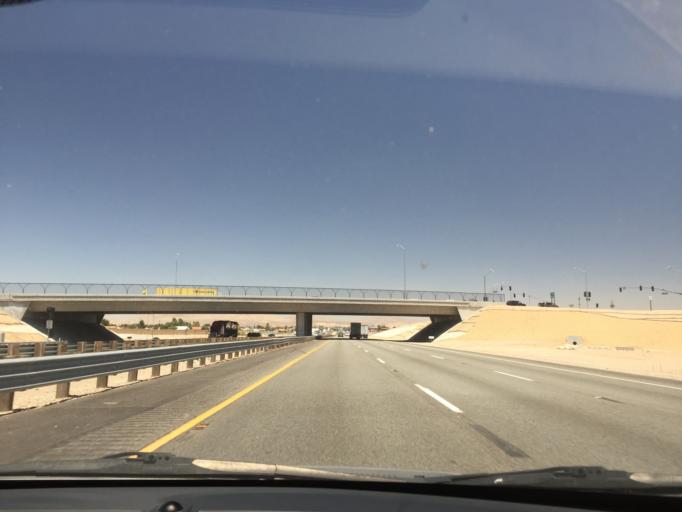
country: US
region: California
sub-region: San Bernardino County
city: Mountain View Acres
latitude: 34.4840
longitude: -117.3362
